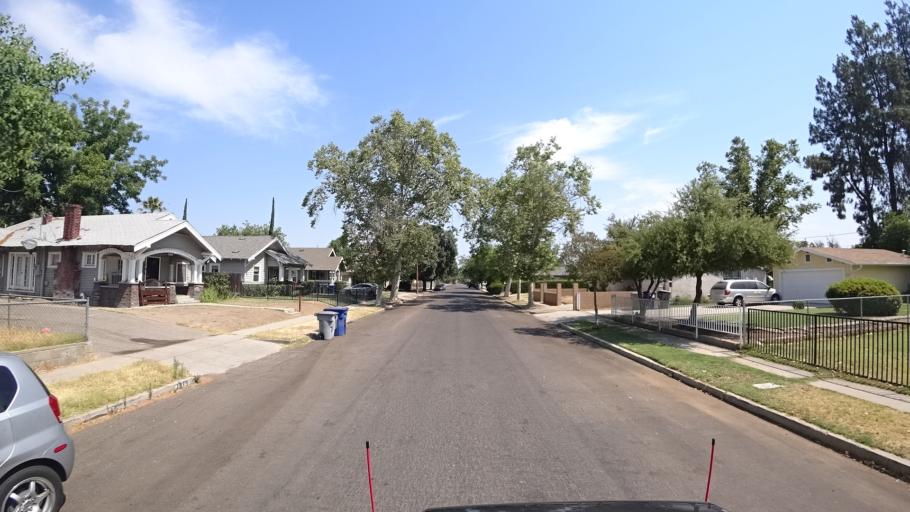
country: US
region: California
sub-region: Fresno County
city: Fresno
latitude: 36.7597
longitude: -119.7945
